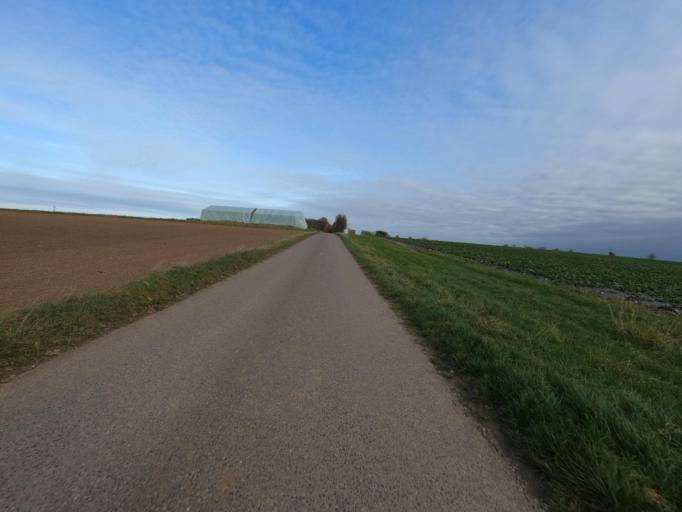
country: DE
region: North Rhine-Westphalia
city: Erkelenz
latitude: 51.0229
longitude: 6.3118
